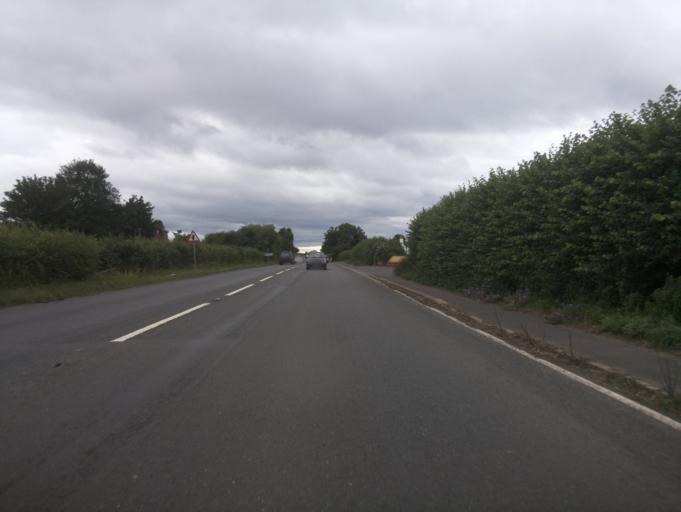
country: GB
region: England
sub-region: Worcestershire
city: Kempsey
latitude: 52.1573
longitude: -2.2146
